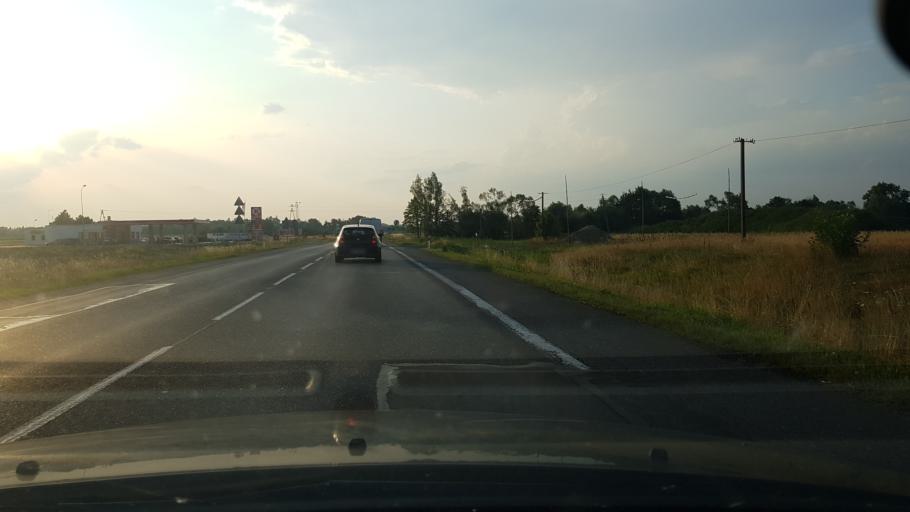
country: PL
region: Masovian Voivodeship
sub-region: Powiat plonski
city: Plonsk
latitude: 52.6968
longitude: 20.3451
